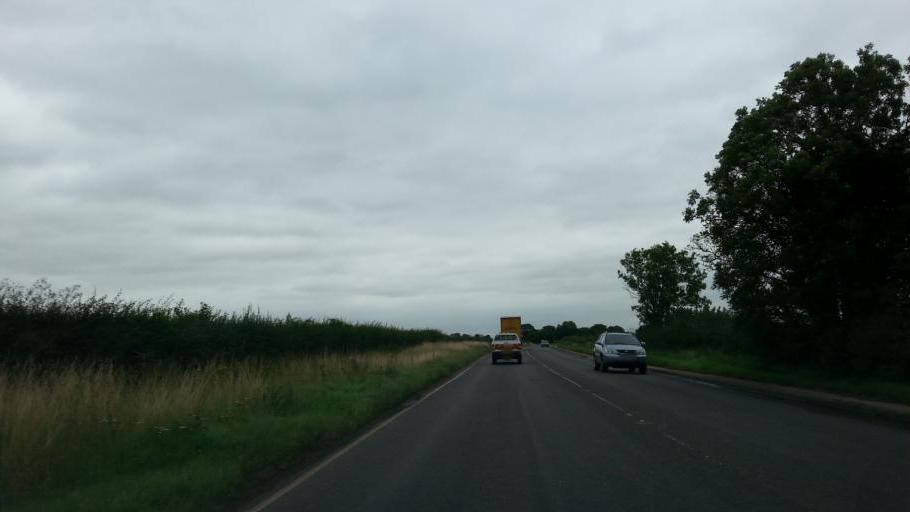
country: GB
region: England
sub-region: Nottinghamshire
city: Newark on Trent
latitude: 53.1110
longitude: -0.8203
